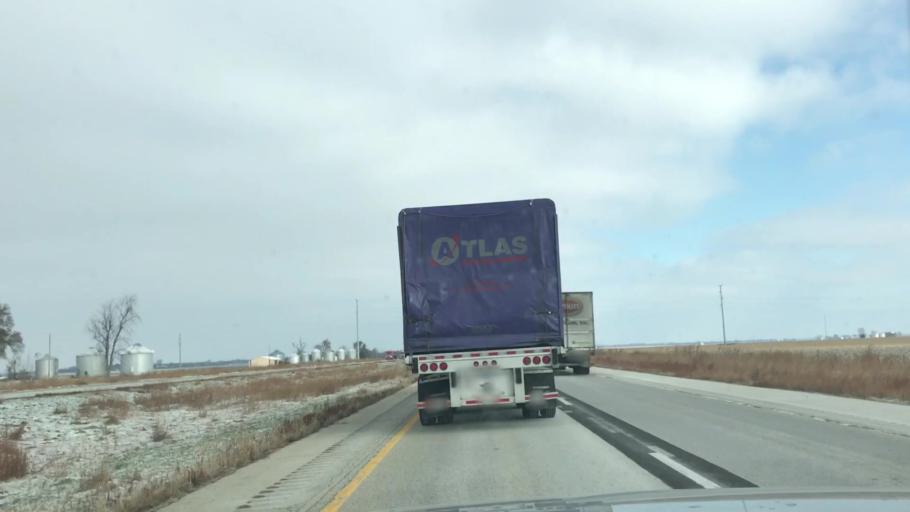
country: US
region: Illinois
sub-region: Sangamon County
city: Divernon
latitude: 39.5259
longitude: -89.6454
